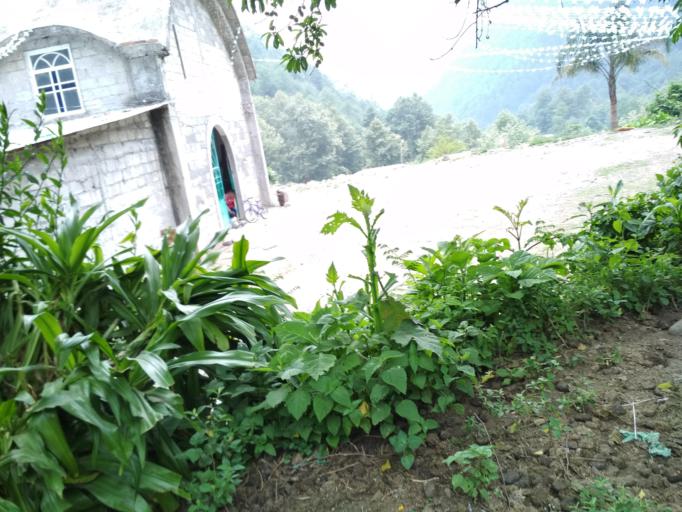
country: MX
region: Veracruz
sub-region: La Perla
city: Metlac Hernandez (Metlac Primero)
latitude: 18.9899
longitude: -97.1203
